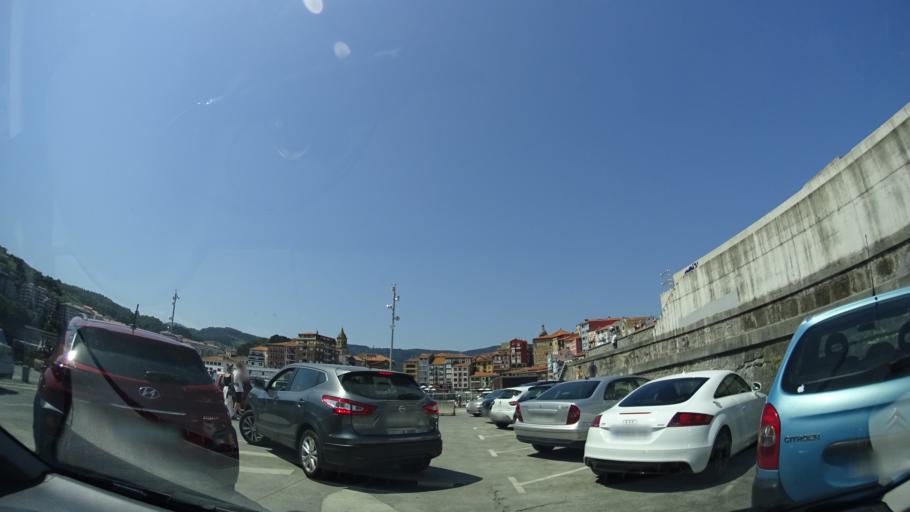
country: ES
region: Basque Country
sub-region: Bizkaia
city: Bermeo
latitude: 43.4205
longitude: -2.7183
